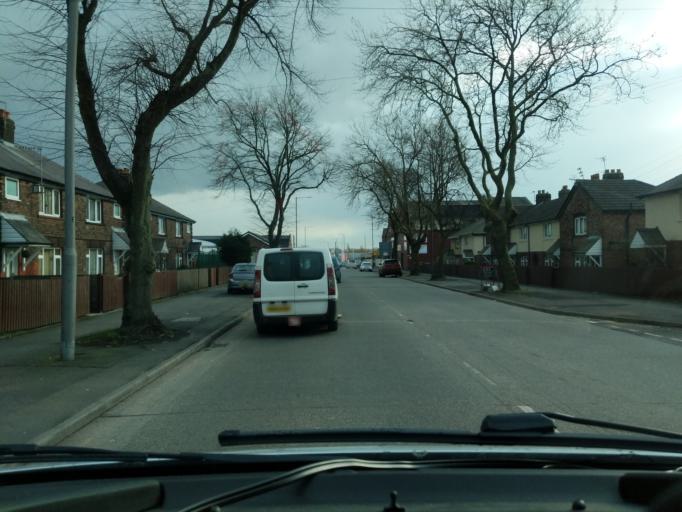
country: GB
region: England
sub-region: St. Helens
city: St Helens
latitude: 53.4526
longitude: -2.7232
